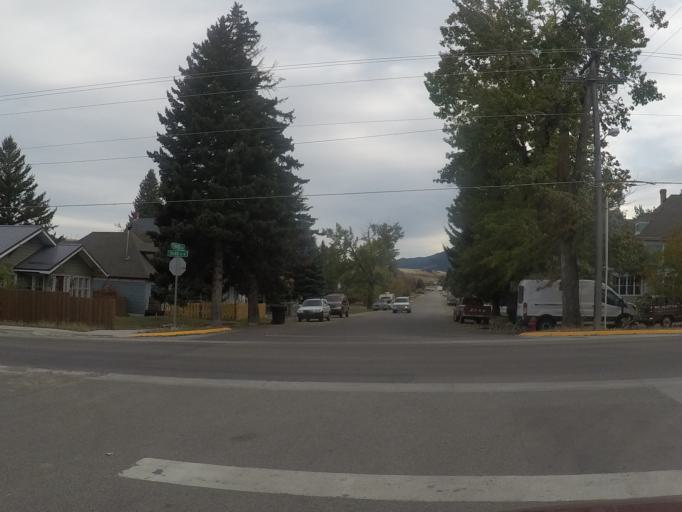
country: US
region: Montana
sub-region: Carbon County
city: Red Lodge
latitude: 45.1949
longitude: -109.2486
